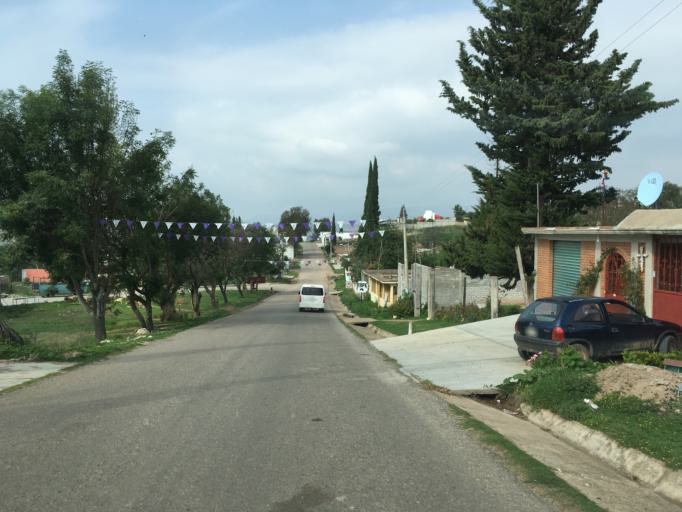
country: MX
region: Oaxaca
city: Magdalena Jaltepec
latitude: 17.3228
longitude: -97.2224
